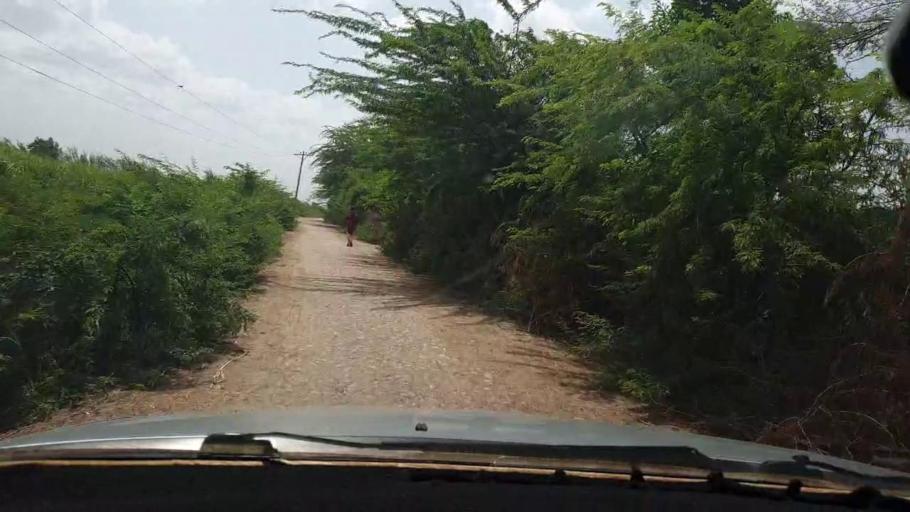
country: PK
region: Sindh
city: Tando Bago
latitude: 24.7562
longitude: 69.1700
